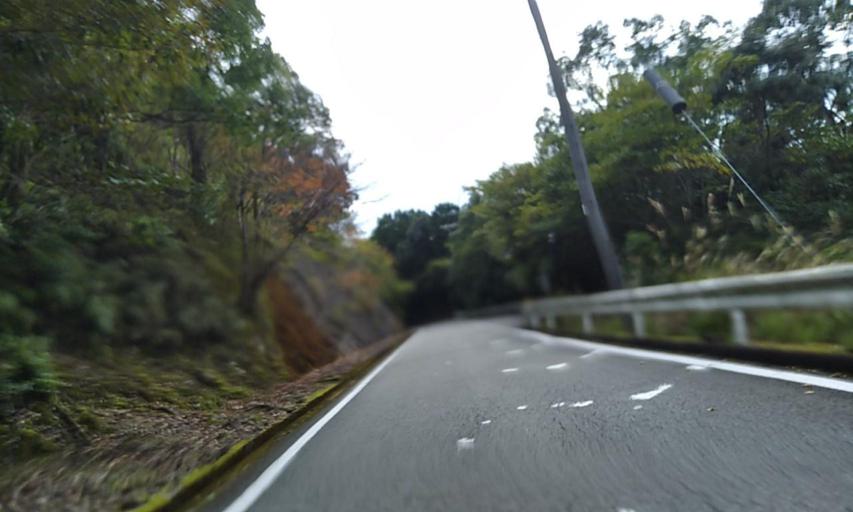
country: JP
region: Wakayama
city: Shingu
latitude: 33.5433
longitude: 135.8312
